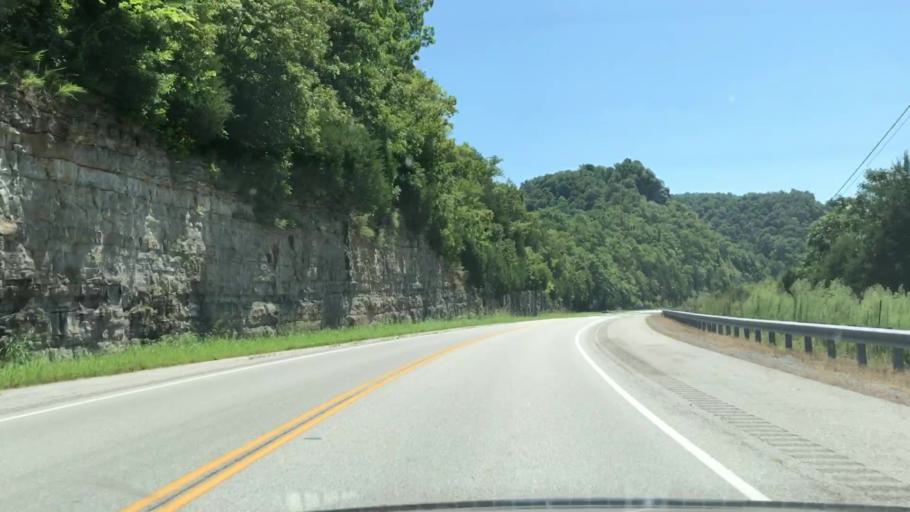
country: US
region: Tennessee
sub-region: Clay County
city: Celina
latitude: 36.4665
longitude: -85.5795
